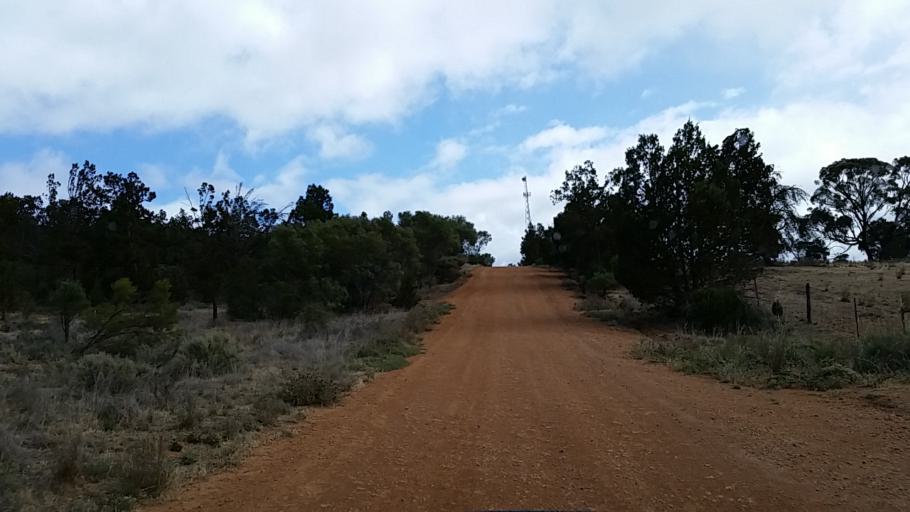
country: AU
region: South Australia
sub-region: Peterborough
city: Peterborough
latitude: -32.9622
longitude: 138.8317
